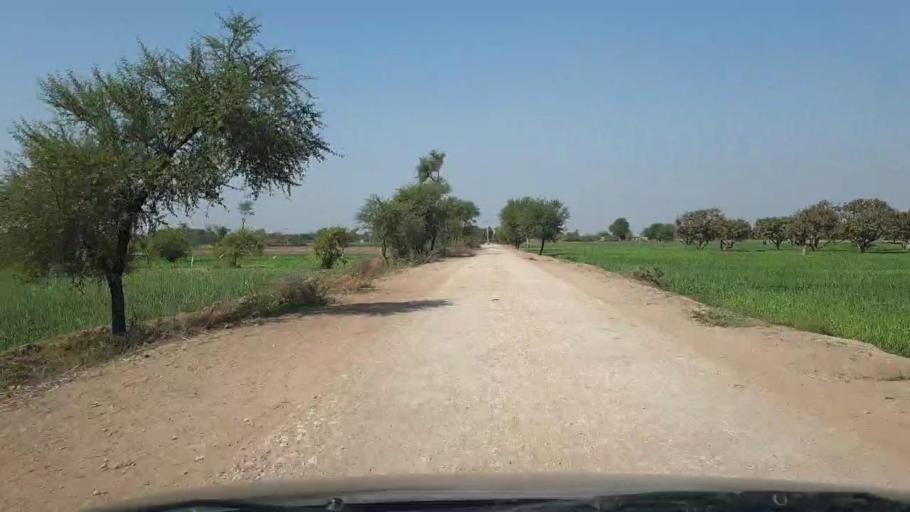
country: PK
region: Sindh
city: Samaro
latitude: 25.2352
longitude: 69.2731
